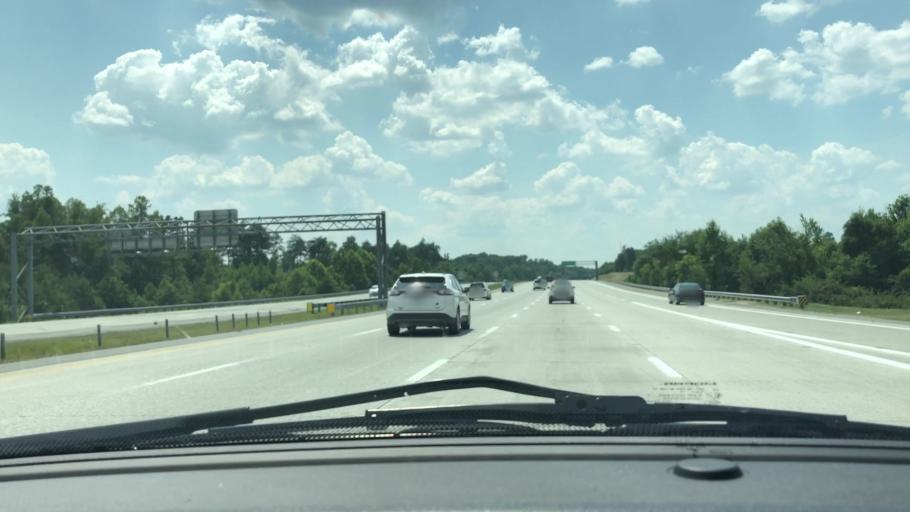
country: US
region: North Carolina
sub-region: Guilford County
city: Pleasant Garden
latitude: 36.0010
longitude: -79.7963
